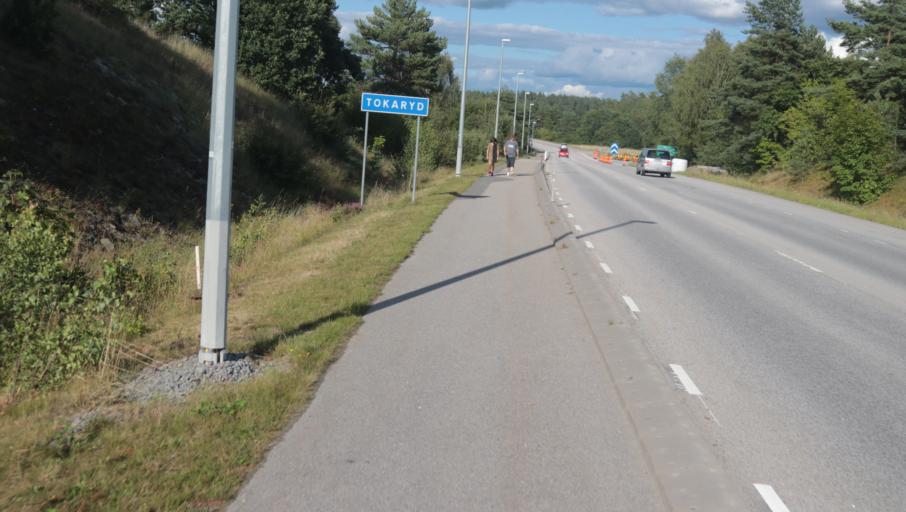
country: SE
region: Blekinge
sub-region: Karlshamns Kommun
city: Karlshamn
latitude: 56.1859
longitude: 14.9220
